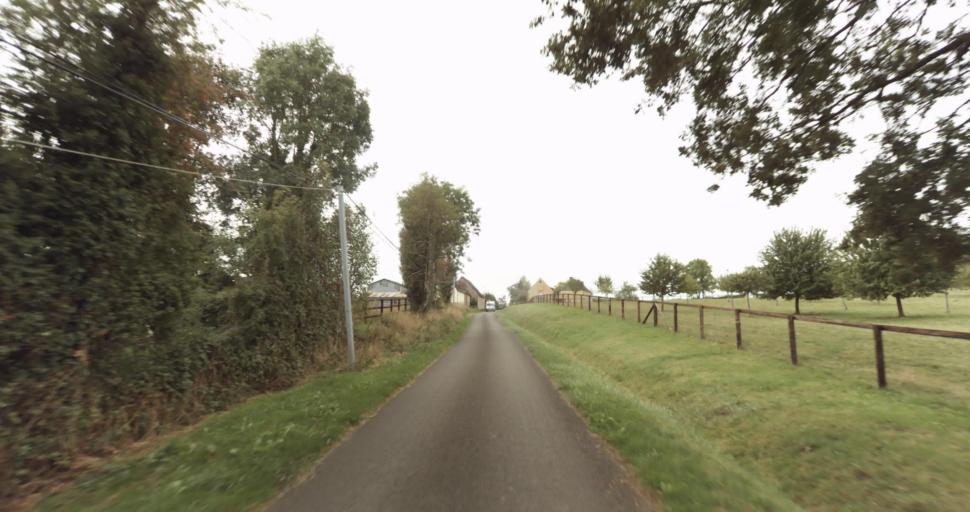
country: FR
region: Lower Normandy
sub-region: Departement de l'Orne
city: Gace
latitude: 48.7359
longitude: 0.2942
